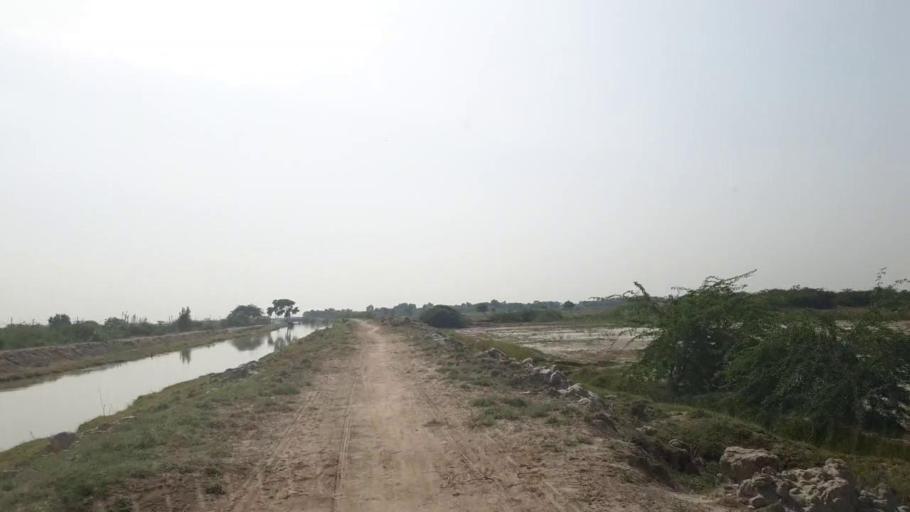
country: PK
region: Sindh
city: Badin
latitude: 24.5577
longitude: 68.8496
